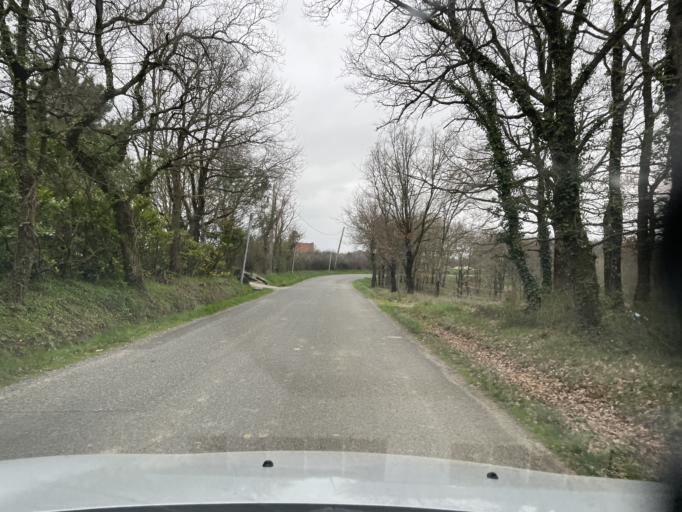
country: FR
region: Midi-Pyrenees
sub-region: Departement du Gers
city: Pujaudran
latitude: 43.6028
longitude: 1.1544
